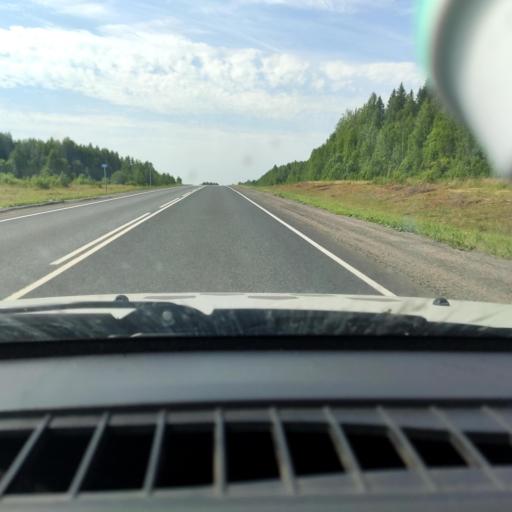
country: RU
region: Kirov
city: Kostino
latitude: 58.7325
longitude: 53.6395
